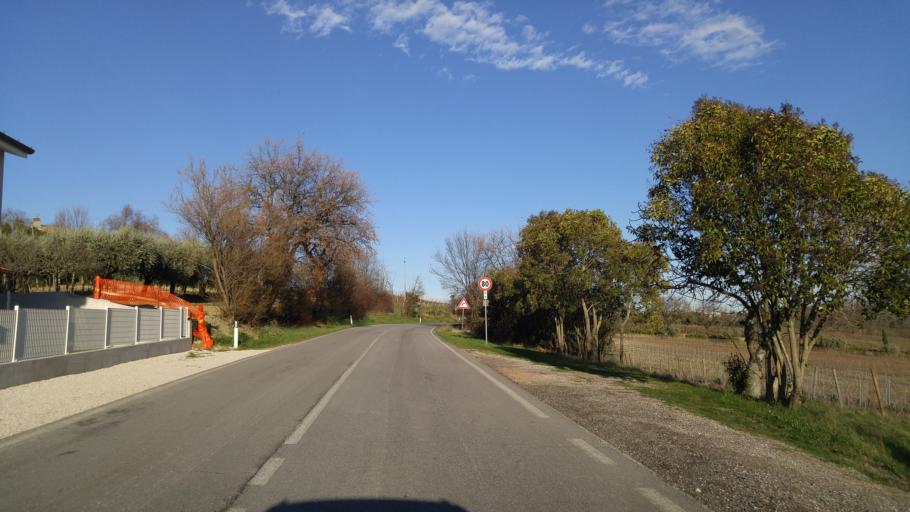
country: IT
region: The Marches
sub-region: Provincia di Pesaro e Urbino
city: Piagge
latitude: 43.7525
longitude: 12.9929
